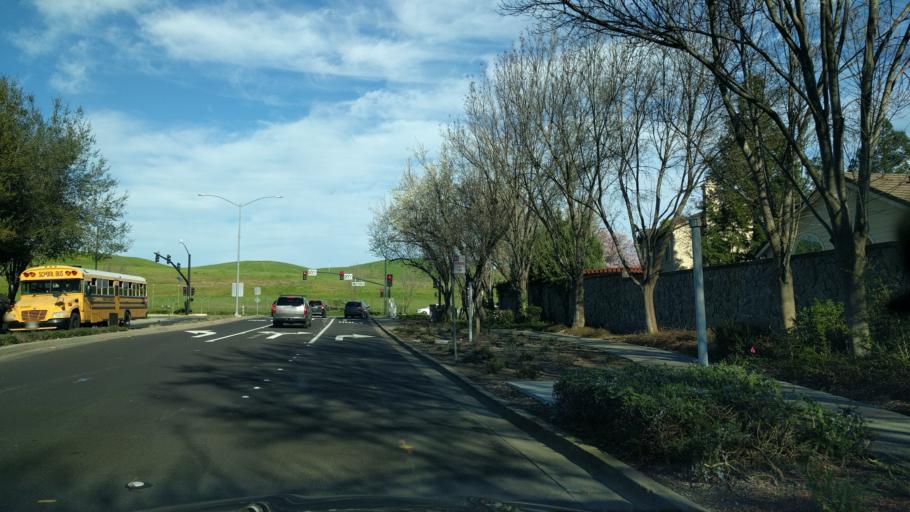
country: US
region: California
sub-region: Alameda County
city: Dublin
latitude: 37.7395
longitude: -121.9150
